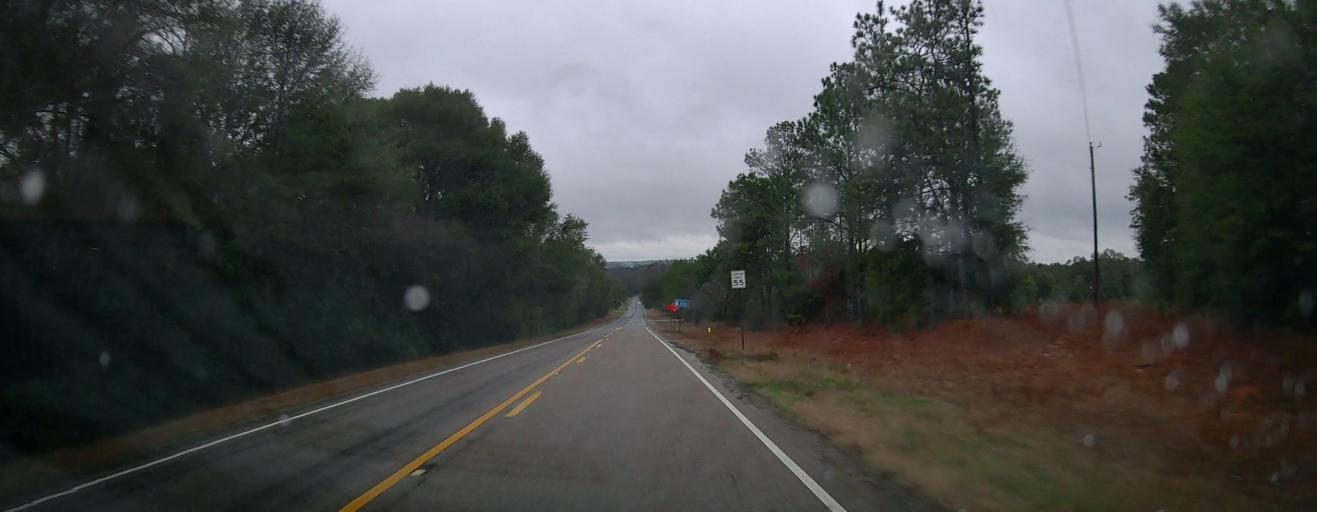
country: US
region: Alabama
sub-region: Autauga County
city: Pine Level
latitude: 32.5528
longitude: -86.6563
